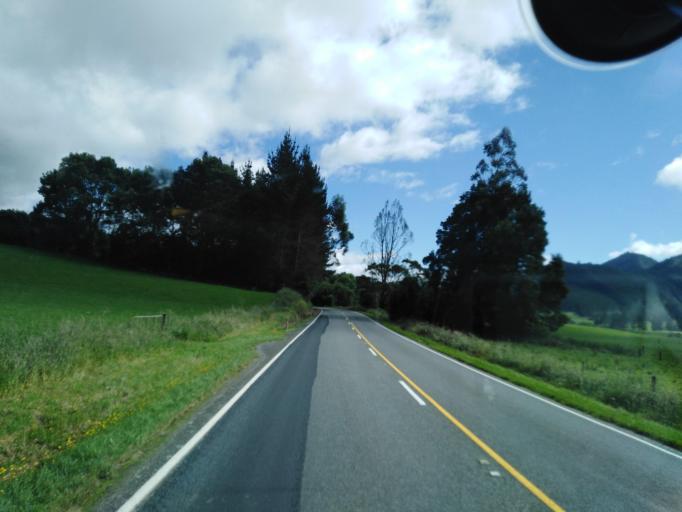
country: NZ
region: Nelson
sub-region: Nelson City
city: Nelson
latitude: -41.2813
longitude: 173.5733
